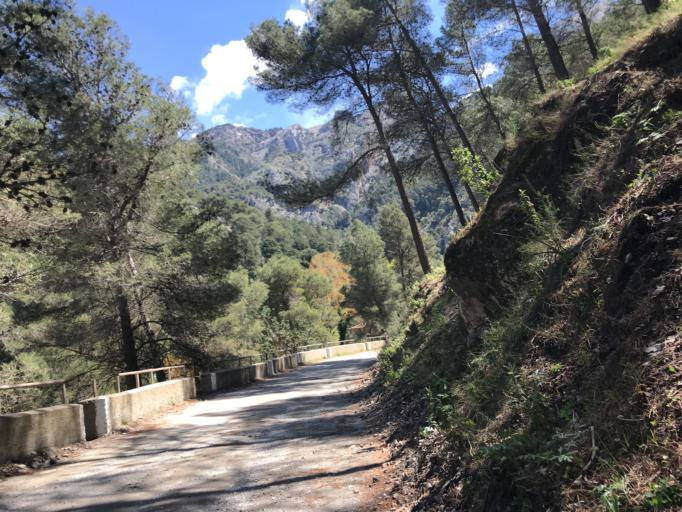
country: ES
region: Andalusia
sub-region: Provincia de Malaga
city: Alcaucin
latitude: 36.9157
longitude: -4.0940
